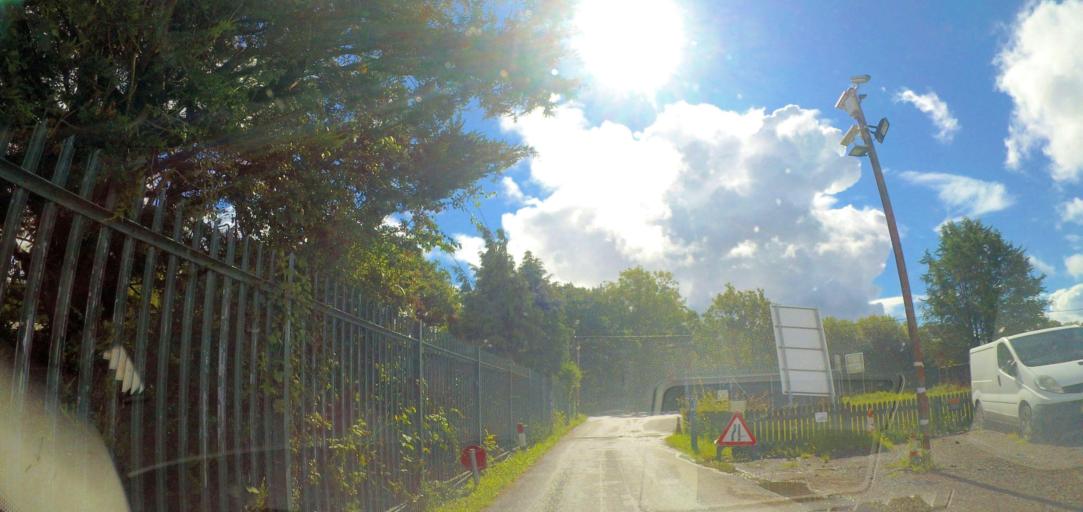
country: GB
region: England
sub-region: Hampshire
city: West End
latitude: 50.9445
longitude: -1.3268
